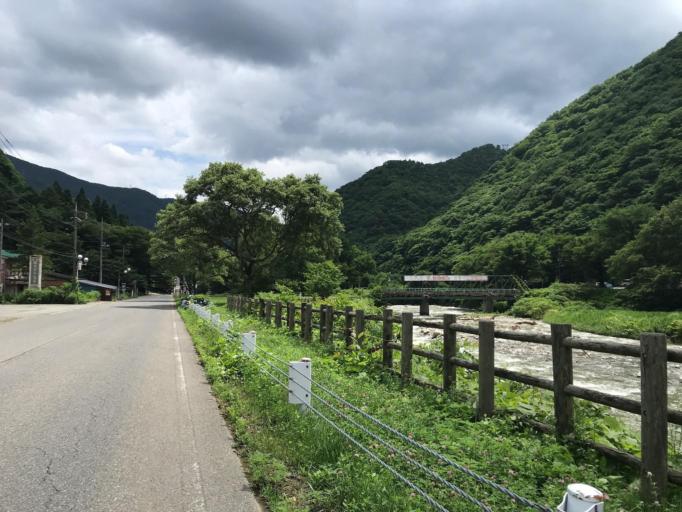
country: JP
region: Gunma
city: Numata
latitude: 36.8114
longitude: 138.9861
